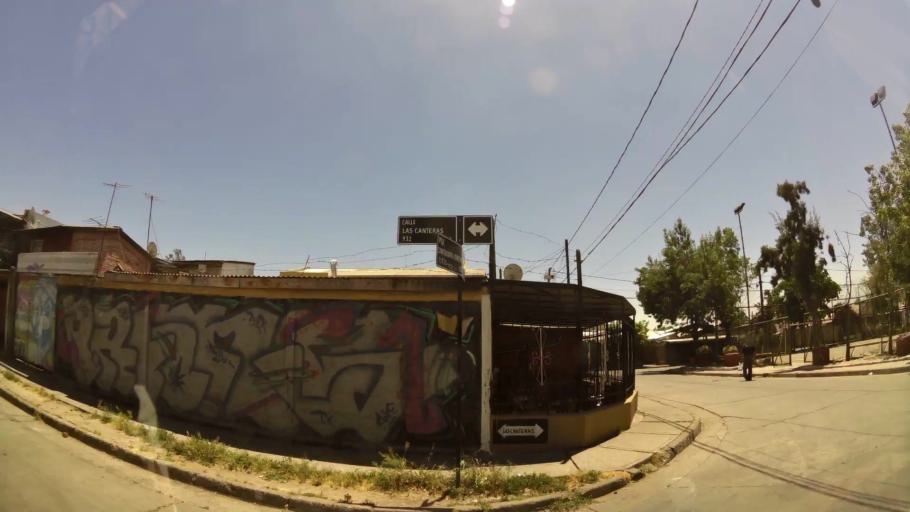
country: CL
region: Santiago Metropolitan
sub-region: Provincia de Santiago
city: La Pintana
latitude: -33.5758
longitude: -70.6650
